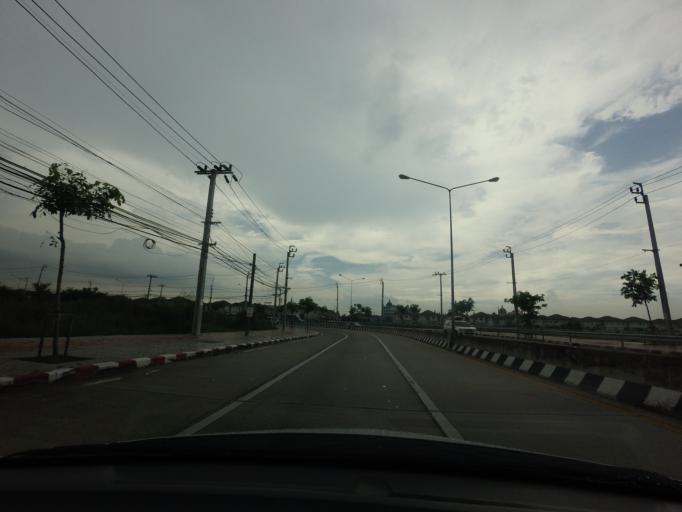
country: TH
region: Bangkok
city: Min Buri
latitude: 13.8202
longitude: 100.7511
